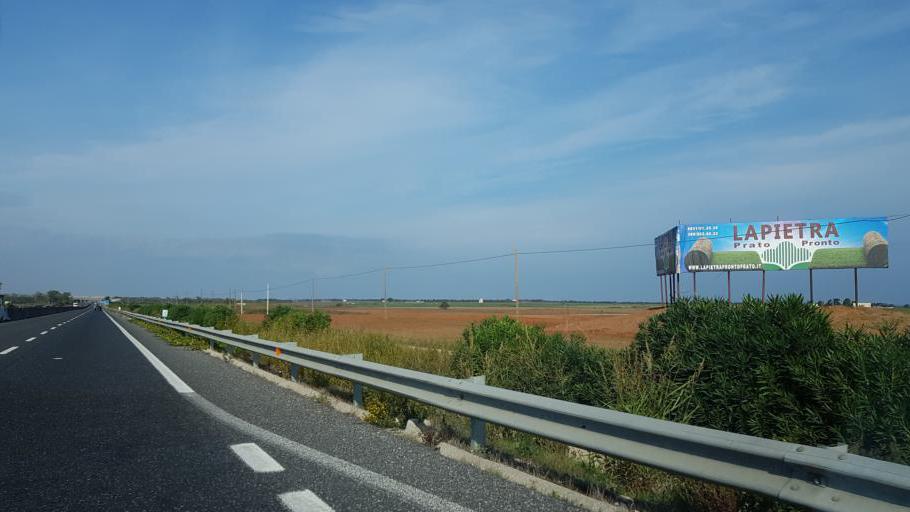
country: IT
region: Apulia
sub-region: Provincia di Brindisi
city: Brindisi
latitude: 40.6718
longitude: 17.8548
